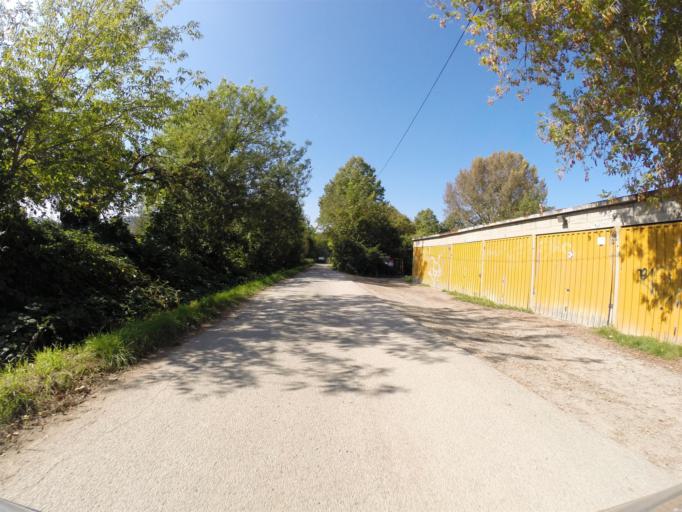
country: DE
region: Thuringia
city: Sulza
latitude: 50.8895
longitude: 11.6035
